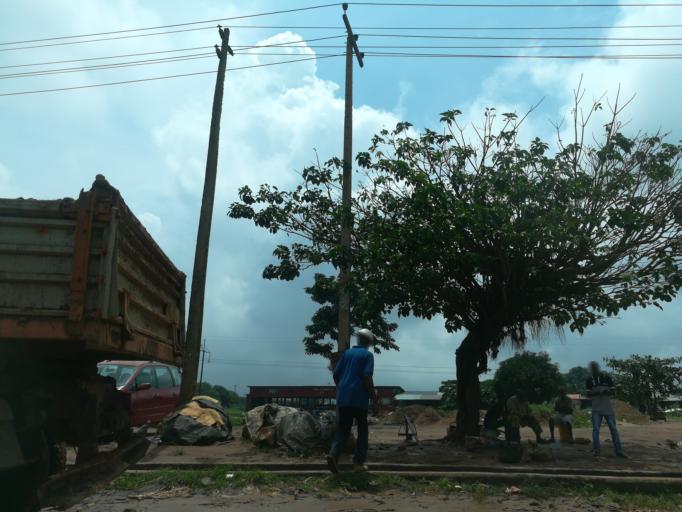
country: NG
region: Lagos
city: Ikorodu
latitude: 6.6773
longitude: 3.5123
